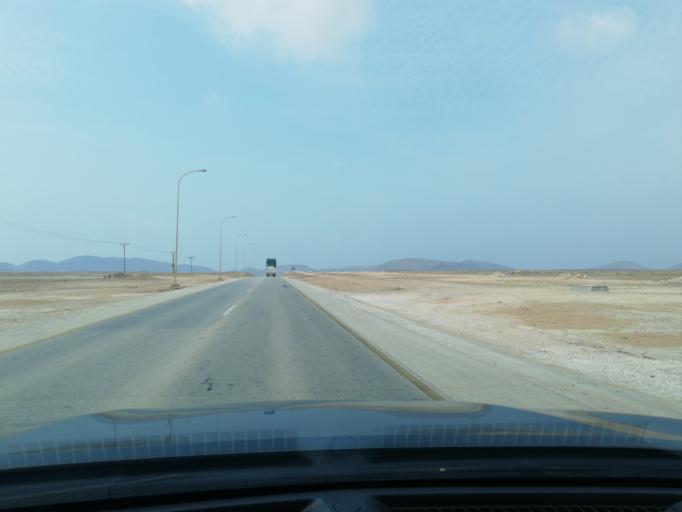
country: OM
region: Zufar
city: Salalah
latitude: 16.9308
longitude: 53.8431
